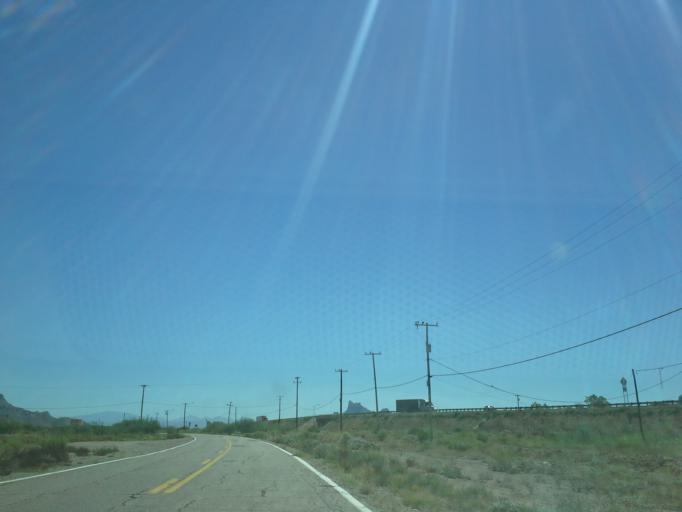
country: US
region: Arizona
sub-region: Pinal County
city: Eloy
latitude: 32.7156
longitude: -111.5007
